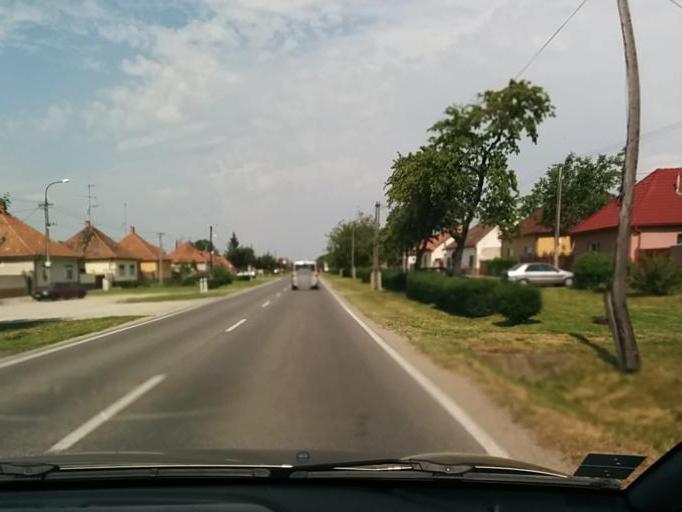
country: SK
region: Trnavsky
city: Sladkovicovo
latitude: 48.1985
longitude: 17.6312
